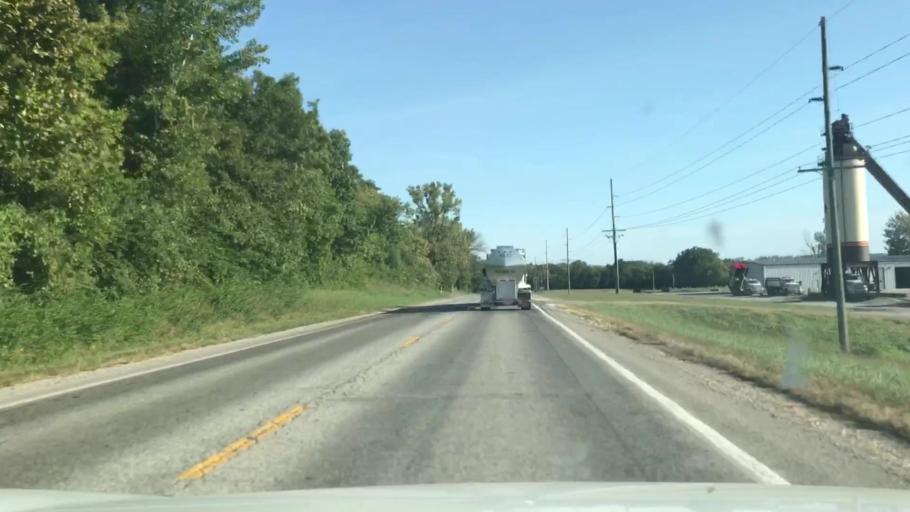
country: US
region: Illinois
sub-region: Adams County
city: Quincy
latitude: 39.8501
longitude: -91.3791
